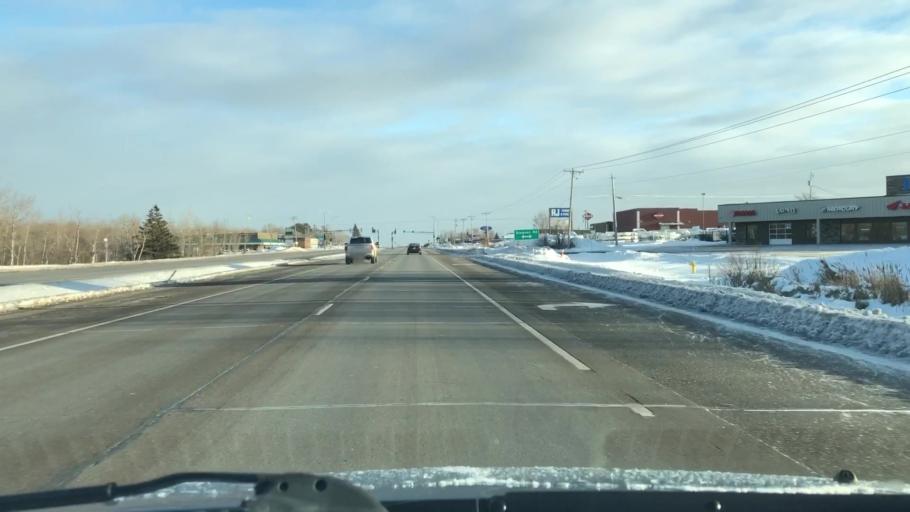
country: US
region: Minnesota
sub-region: Saint Louis County
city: Hermantown
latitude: 46.8294
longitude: -92.1988
